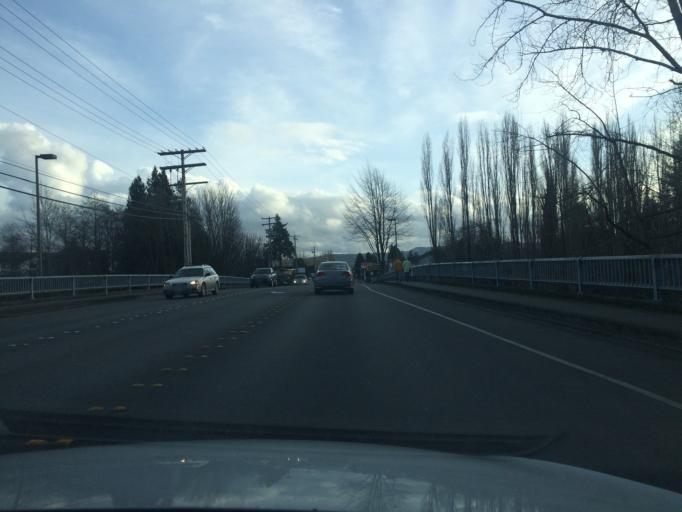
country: US
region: Washington
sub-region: Whatcom County
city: Bellingham
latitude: 48.7738
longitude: -122.4957
